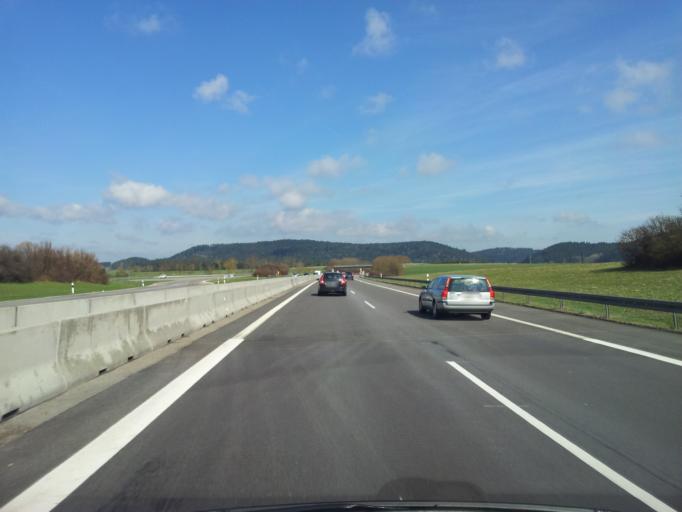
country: DE
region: Baden-Wuerttemberg
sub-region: Freiburg Region
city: Epfendorf
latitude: 48.2626
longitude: 8.6399
